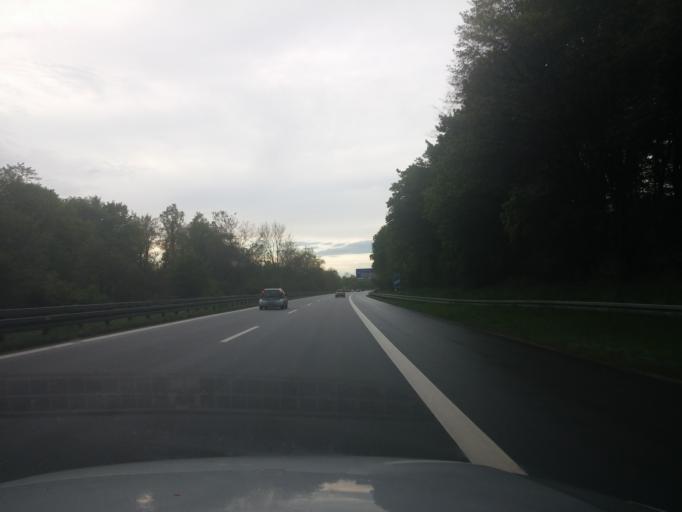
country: DE
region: Bavaria
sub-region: Upper Bavaria
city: Taufkirchen
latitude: 48.0501
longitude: 11.5959
